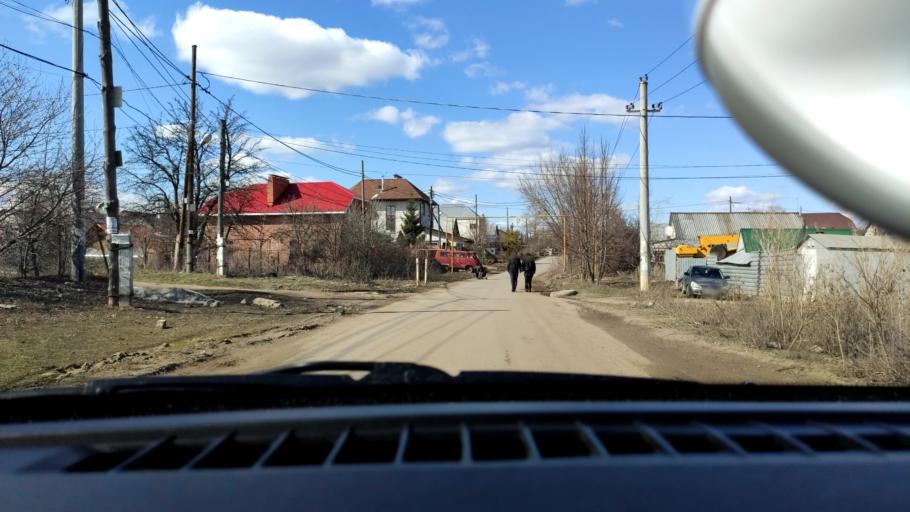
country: RU
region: Samara
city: Petra-Dubrava
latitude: 53.2933
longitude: 50.3101
